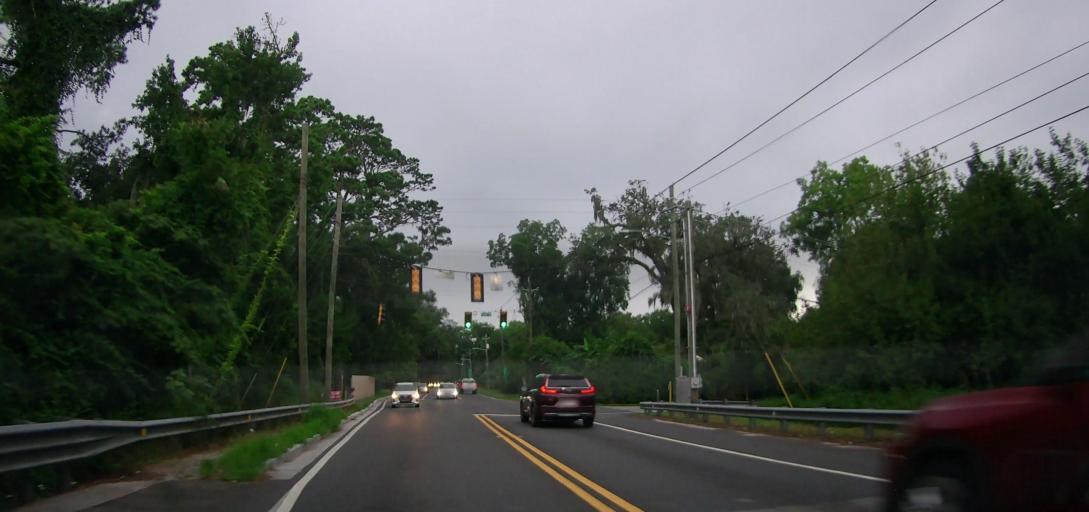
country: US
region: Georgia
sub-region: Glynn County
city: Dock Junction
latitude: 31.2223
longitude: -81.5044
